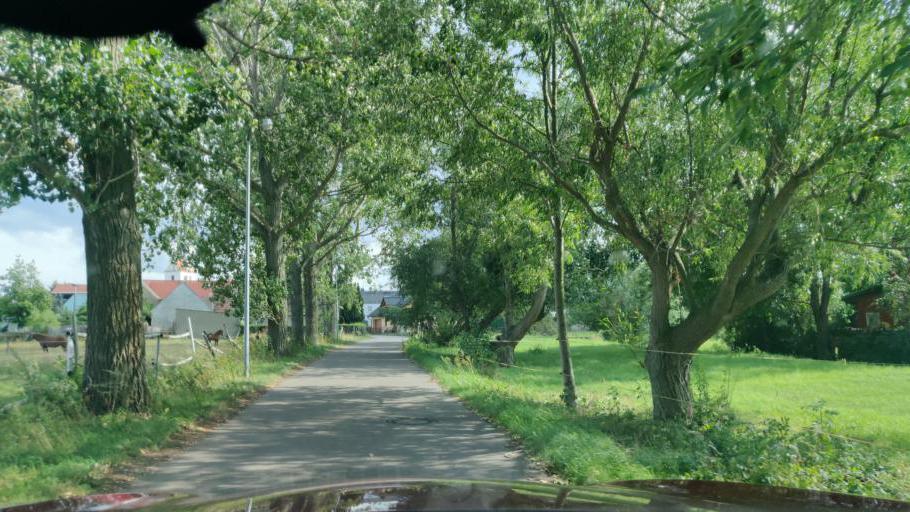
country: DE
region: Saxony
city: Schildau
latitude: 51.4928
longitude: 12.9007
